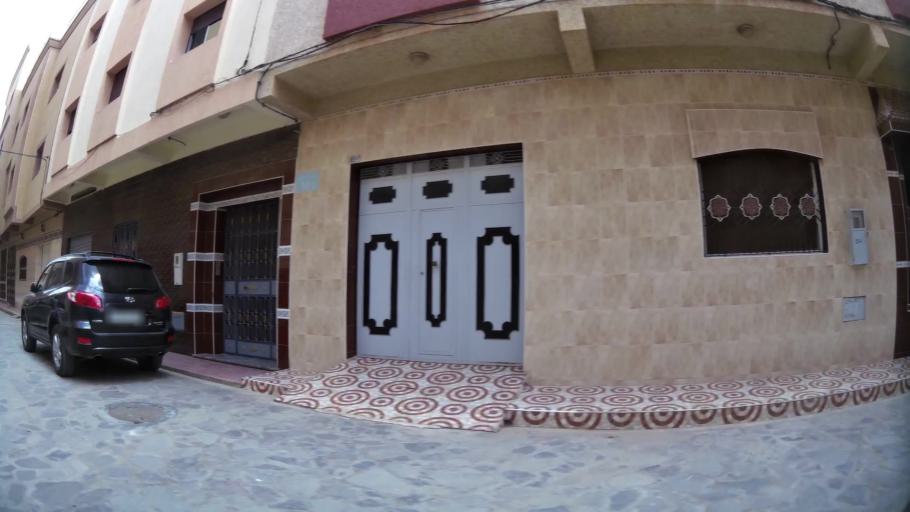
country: MA
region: Oriental
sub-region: Nador
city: Nador
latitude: 35.1676
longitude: -2.9231
